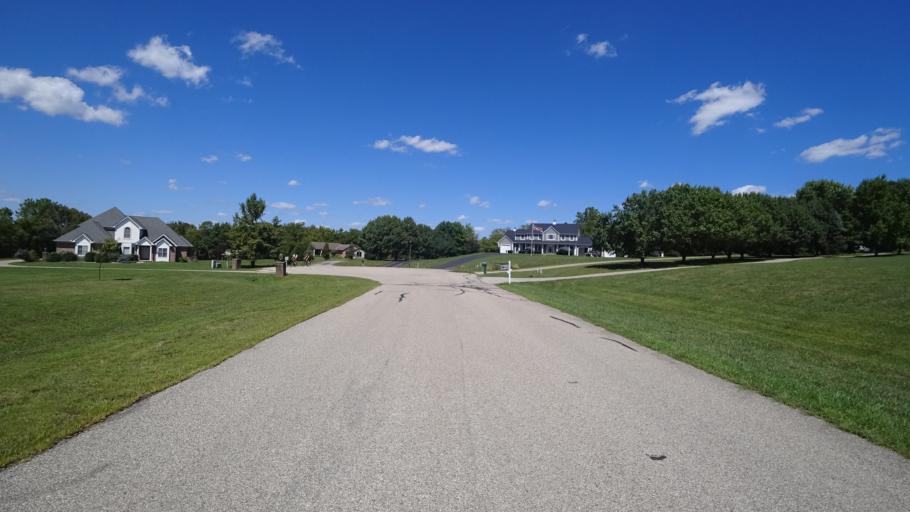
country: US
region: Ohio
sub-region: Butler County
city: New Miami
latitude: 39.4126
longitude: -84.5231
